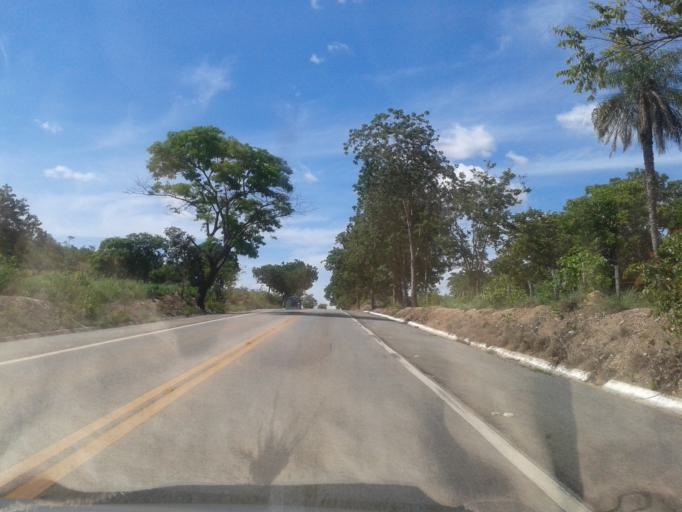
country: BR
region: Goias
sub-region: Itapuranga
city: Itapuranga
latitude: -15.4265
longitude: -50.3746
